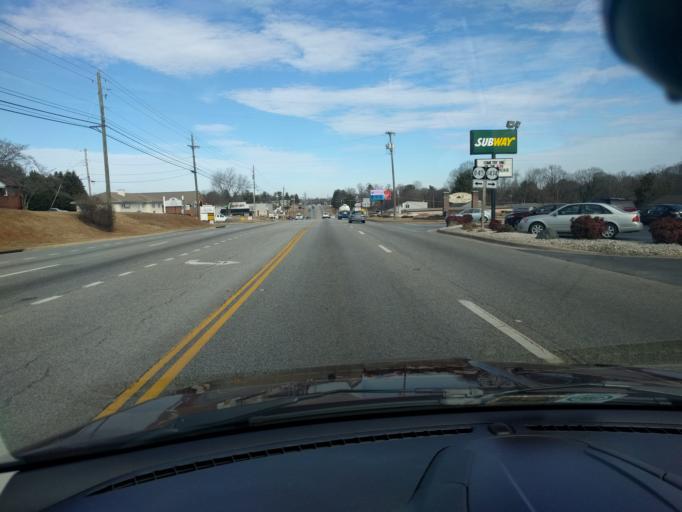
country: US
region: Virginia
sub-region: Bedford County
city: Forest
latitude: 37.3858
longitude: -79.2423
